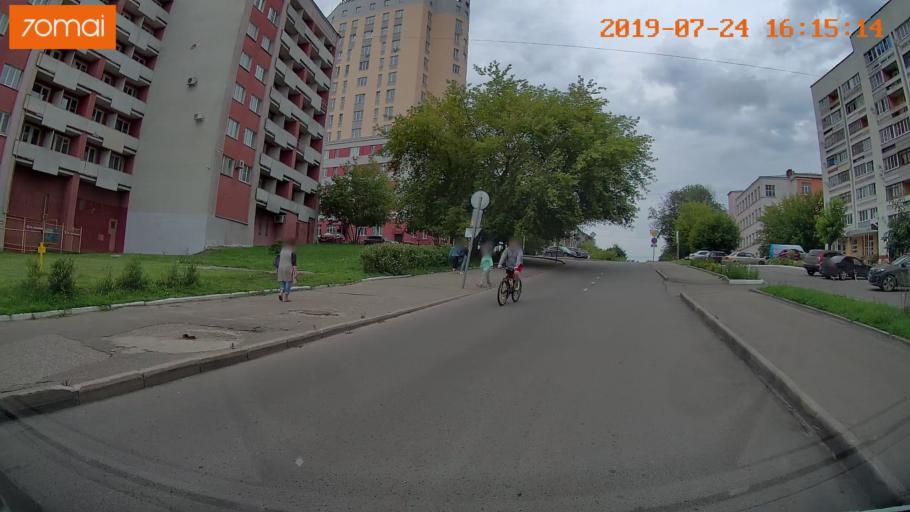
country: RU
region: Ivanovo
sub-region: Gorod Ivanovo
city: Ivanovo
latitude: 57.0044
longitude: 40.9800
